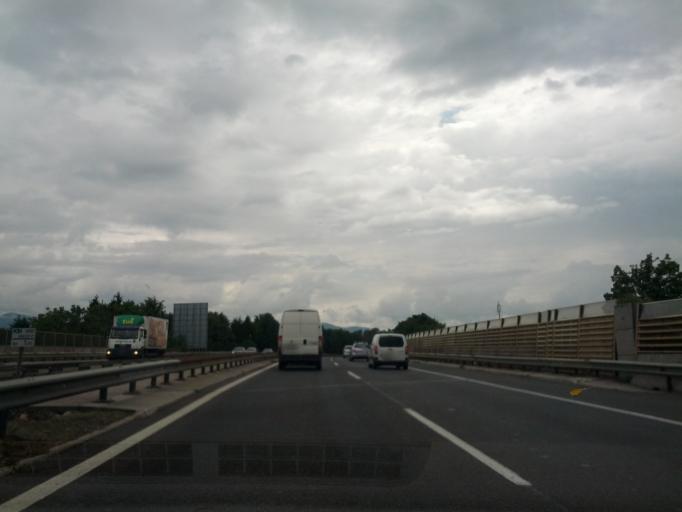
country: SI
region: Brezovica
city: Vnanje Gorice
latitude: 46.0324
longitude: 14.4466
